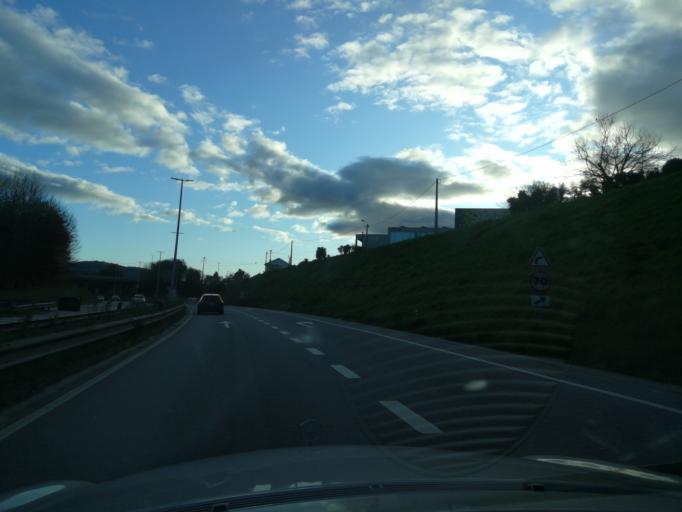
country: PT
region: Braga
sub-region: Barcelos
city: Vila Frescainha
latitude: 41.5333
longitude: -8.6397
